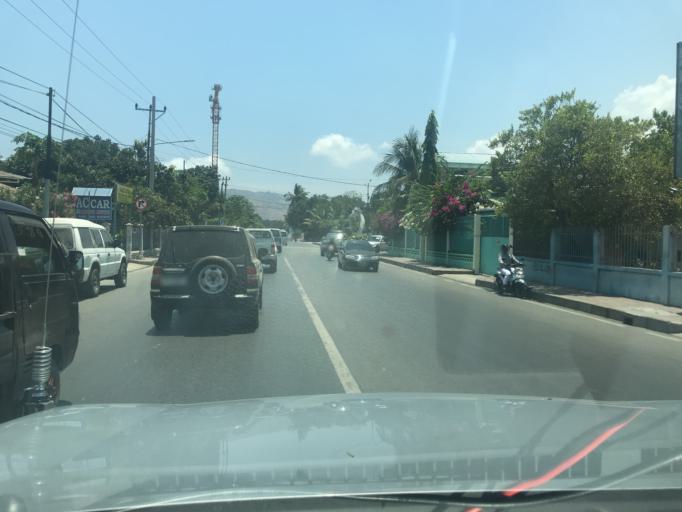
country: TL
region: Dili
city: Dili
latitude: -8.5542
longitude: 125.5678
